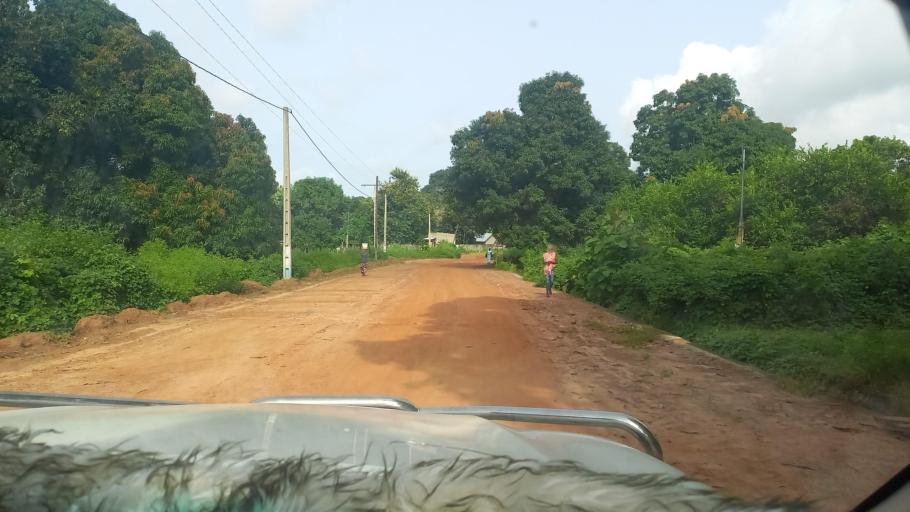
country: SN
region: Ziguinchor
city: Ziguinchor
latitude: 12.6632
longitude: -16.2634
